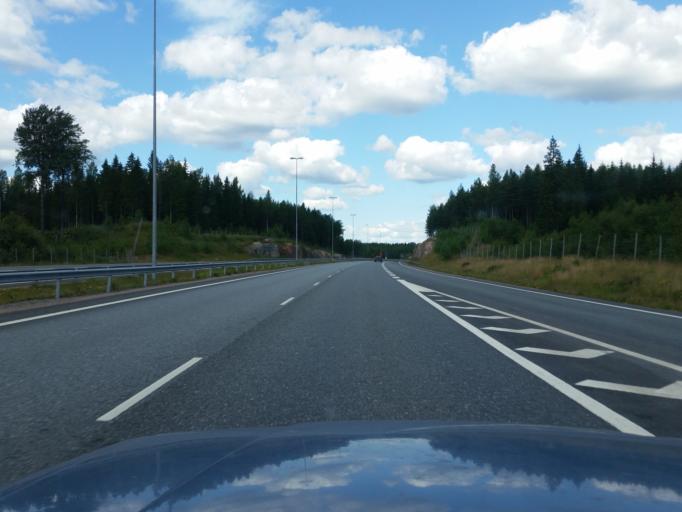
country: FI
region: Uusimaa
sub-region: Helsinki
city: Saukkola
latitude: 60.3449
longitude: 23.9073
